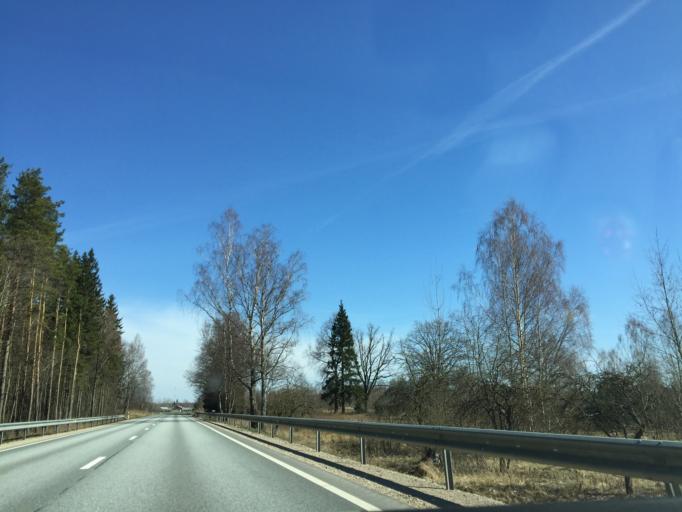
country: LV
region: Valmieras Rajons
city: Valmiera
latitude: 57.5649
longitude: 25.4614
